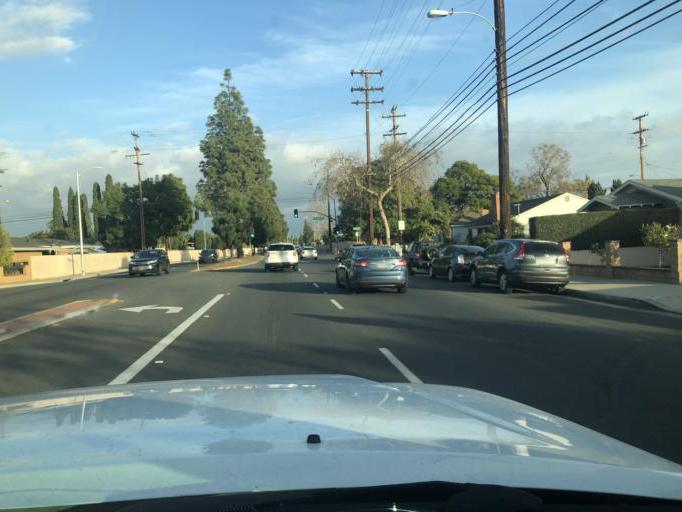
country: US
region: California
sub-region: Orange County
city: Santa Ana
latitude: 33.7272
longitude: -117.8644
